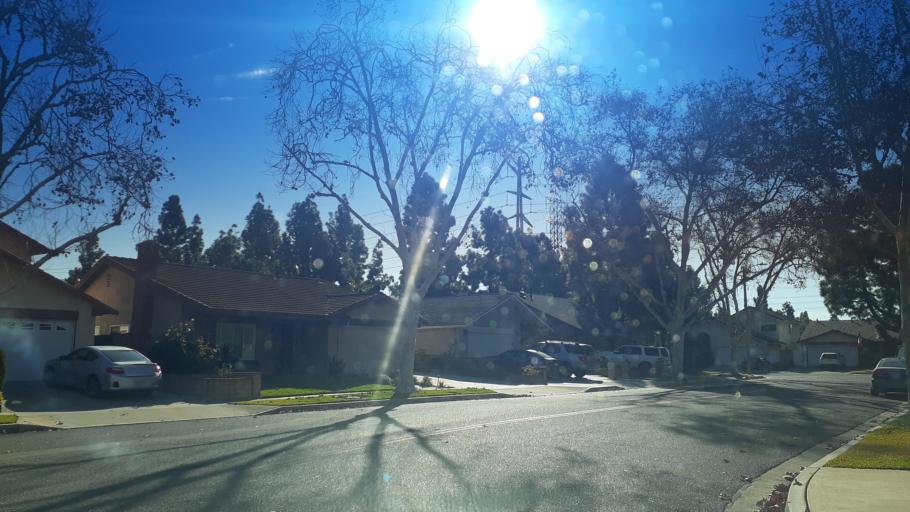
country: US
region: California
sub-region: Los Angeles County
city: Cerritos
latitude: 33.8513
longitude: -118.0684
